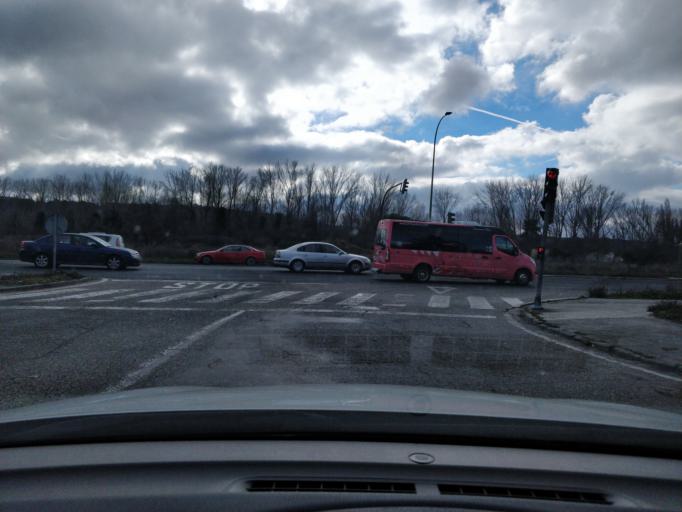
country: ES
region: Castille and Leon
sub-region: Provincia de Burgos
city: Burgos
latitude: 42.3463
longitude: -3.6586
